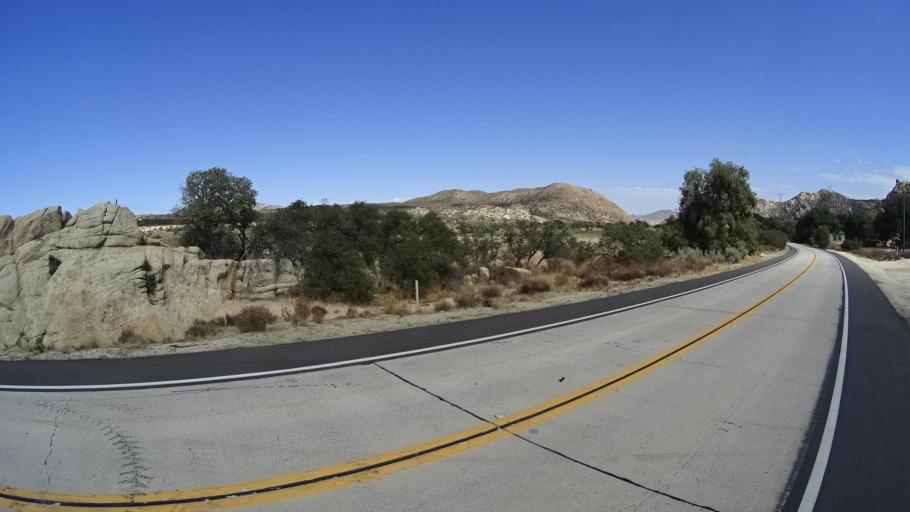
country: MX
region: Baja California
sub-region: Tecate
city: Cereso del Hongo
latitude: 32.6619
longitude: -116.2577
